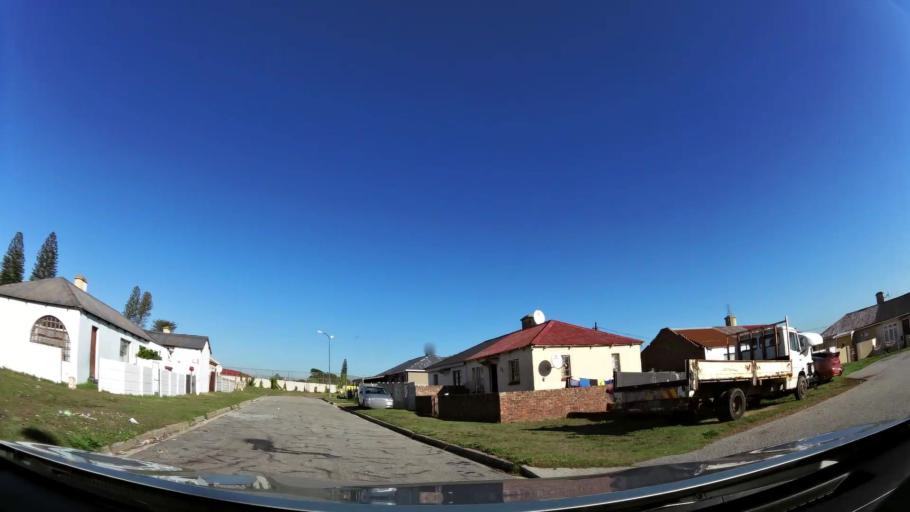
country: ZA
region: Eastern Cape
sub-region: Nelson Mandela Bay Metropolitan Municipality
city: Port Elizabeth
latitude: -33.9838
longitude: 25.6311
